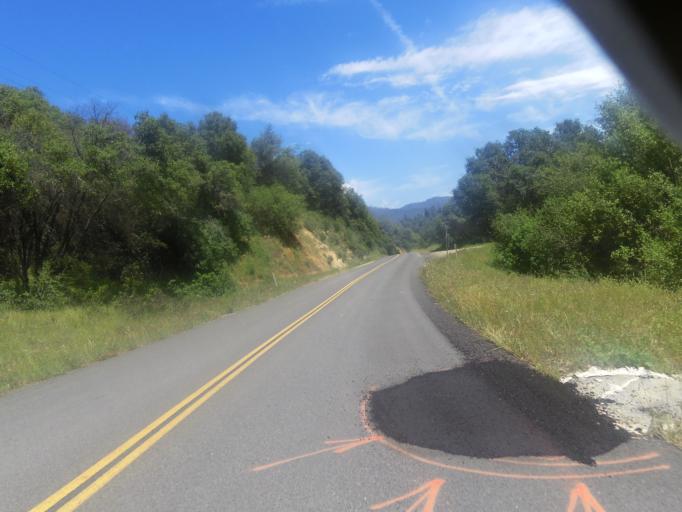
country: US
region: California
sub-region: Mariposa County
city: Midpines
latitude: 37.5124
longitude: -119.8532
